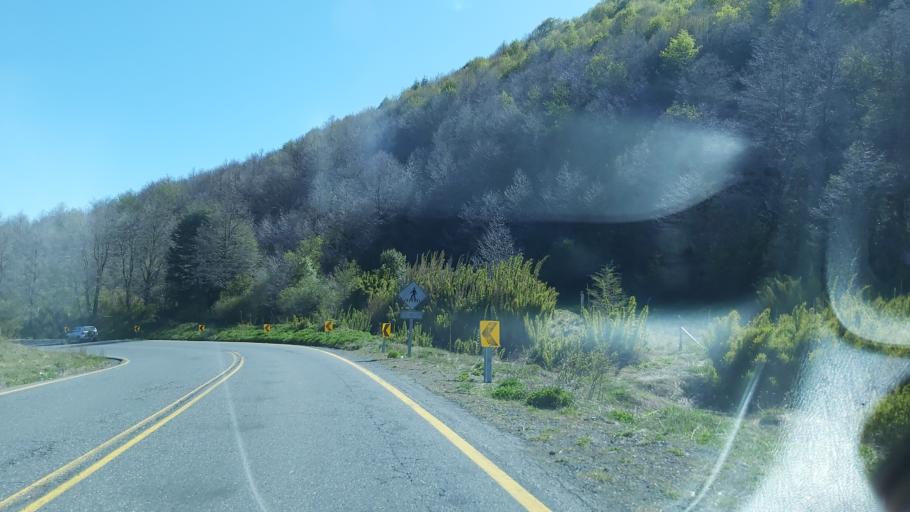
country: CL
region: Araucania
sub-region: Provincia de Cautin
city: Vilcun
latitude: -38.4648
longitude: -71.6375
